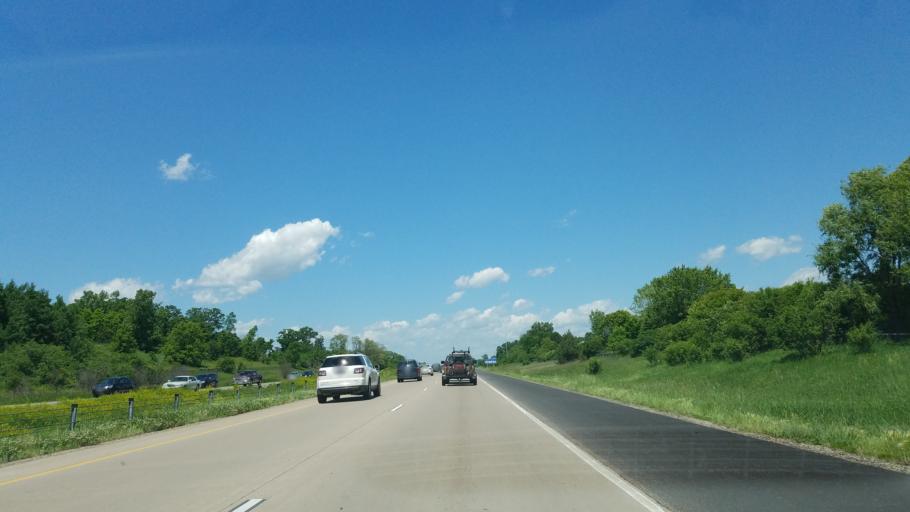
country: US
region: Minnesota
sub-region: Ramsey County
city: North Saint Paul
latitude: 45.0153
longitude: -92.9586
